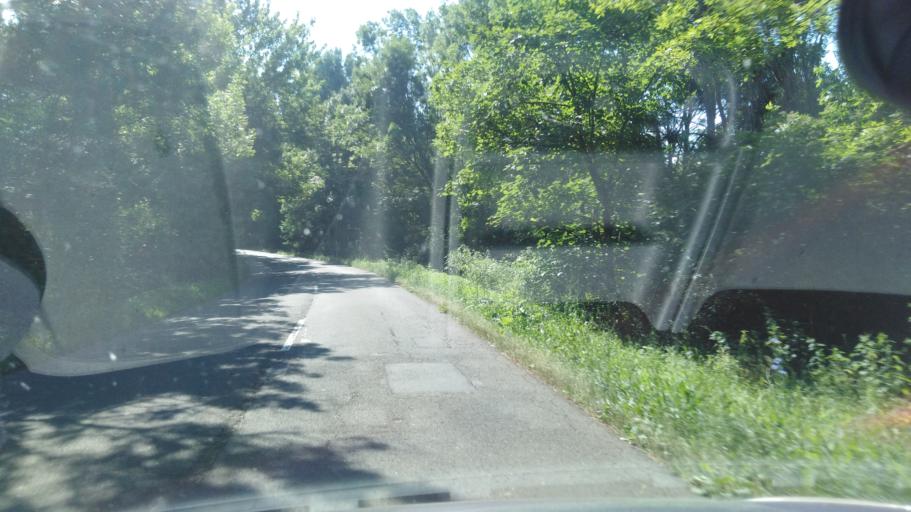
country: HU
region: Nograd
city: Retsag
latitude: 47.9377
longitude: 19.1524
